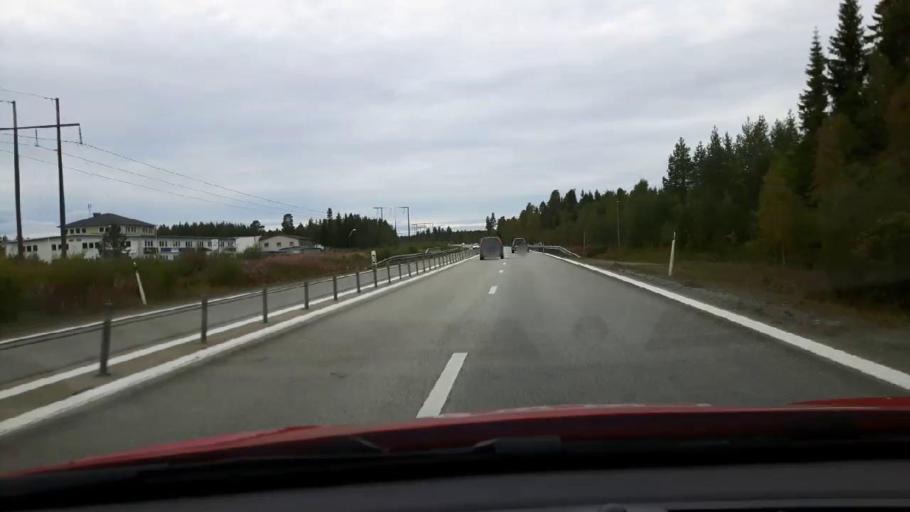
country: SE
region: Jaemtland
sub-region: OEstersunds Kommun
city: Brunflo
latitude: 63.1575
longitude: 14.7622
